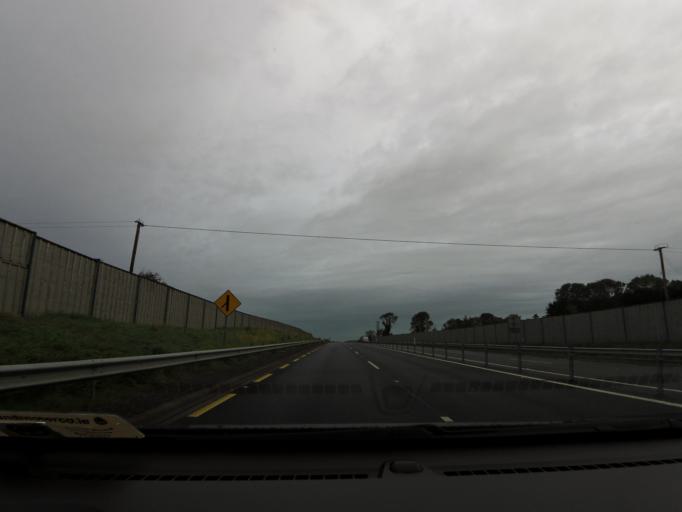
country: IE
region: Connaught
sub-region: County Galway
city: Tuam
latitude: 53.5122
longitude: -8.8787
